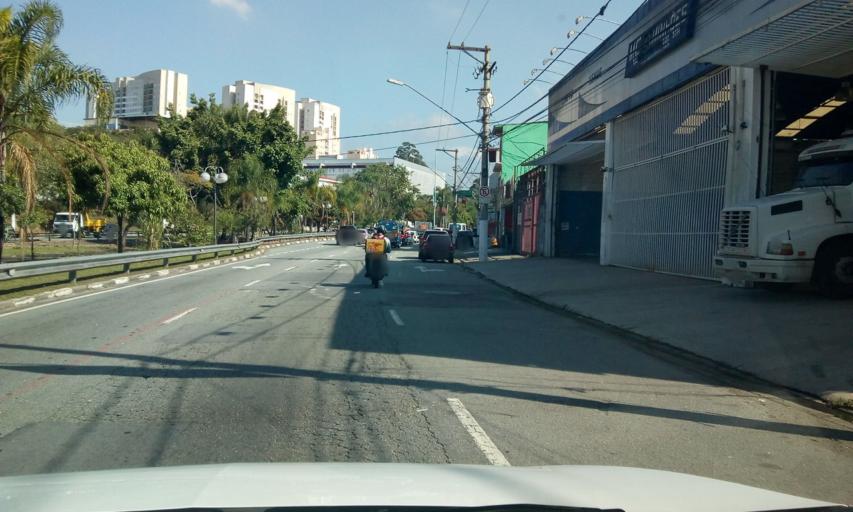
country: BR
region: Sao Paulo
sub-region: Osasco
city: Osasco
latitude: -23.5513
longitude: -46.7774
